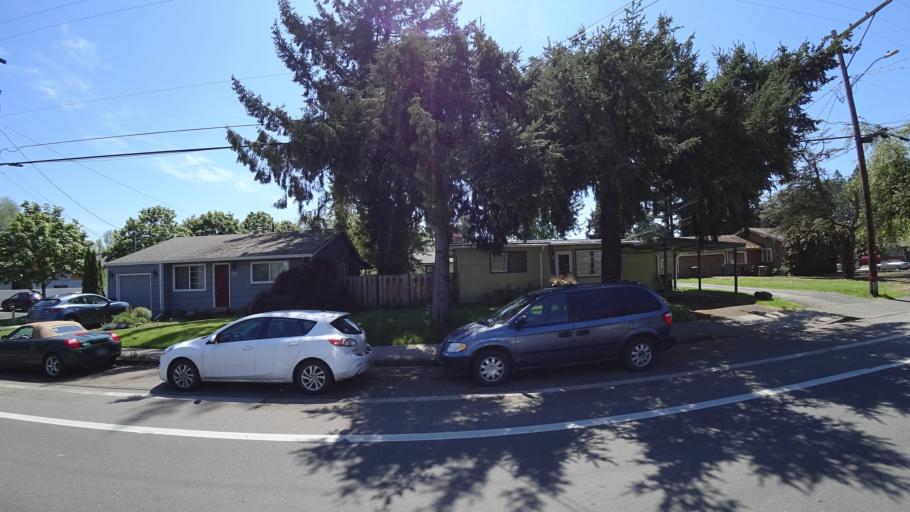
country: US
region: Oregon
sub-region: Washington County
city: Hillsboro
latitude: 45.5149
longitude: -122.9716
